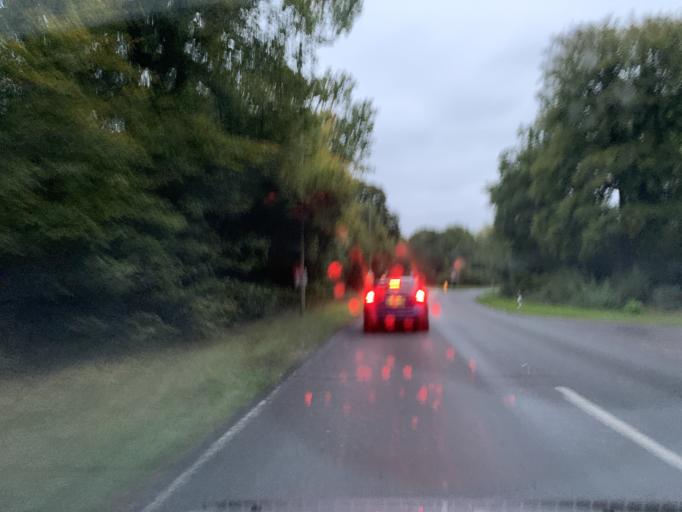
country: GB
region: England
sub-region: Hampshire
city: Cadnam
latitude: 50.9195
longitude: -1.5821
